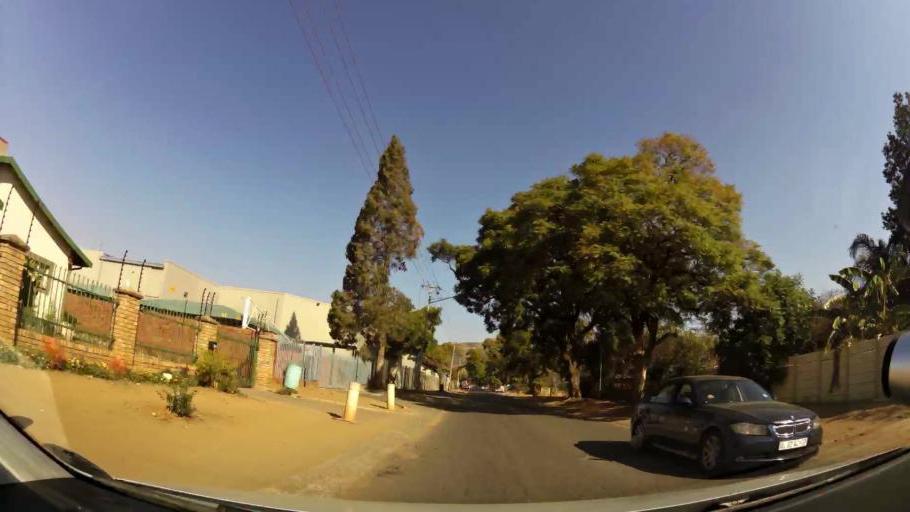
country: ZA
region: Gauteng
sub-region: City of Tshwane Metropolitan Municipality
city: Pretoria
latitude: -25.6728
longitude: 28.1728
